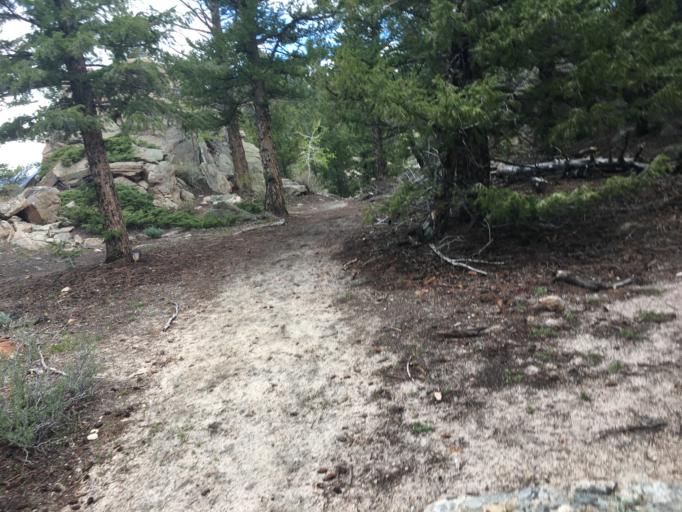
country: US
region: Colorado
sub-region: Larimer County
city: Estes Park
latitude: 40.3401
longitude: -105.5890
